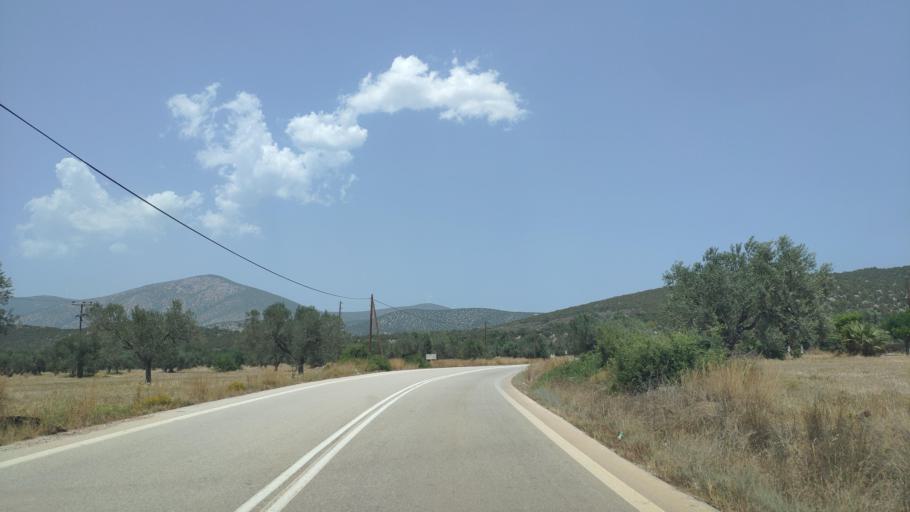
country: GR
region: Peloponnese
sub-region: Nomos Argolidos
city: Koilas
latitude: 37.4174
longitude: 23.1528
